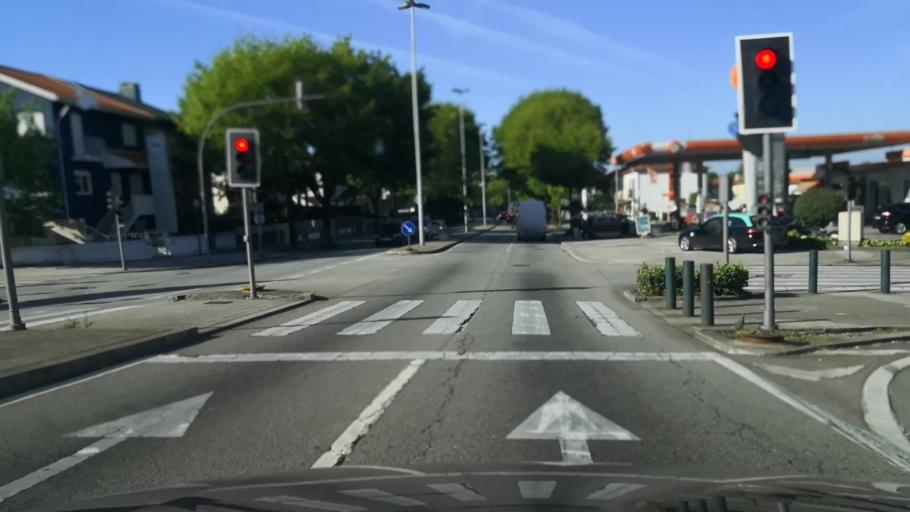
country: PT
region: Porto
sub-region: Maia
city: Pedroucos
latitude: 41.1689
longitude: -8.5873
